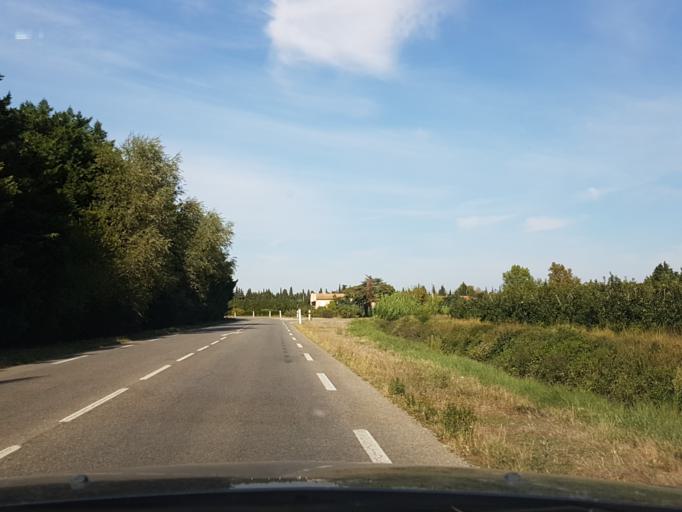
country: FR
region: Provence-Alpes-Cote d'Azur
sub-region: Departement des Bouches-du-Rhone
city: Noves
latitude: 43.8603
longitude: 4.9025
